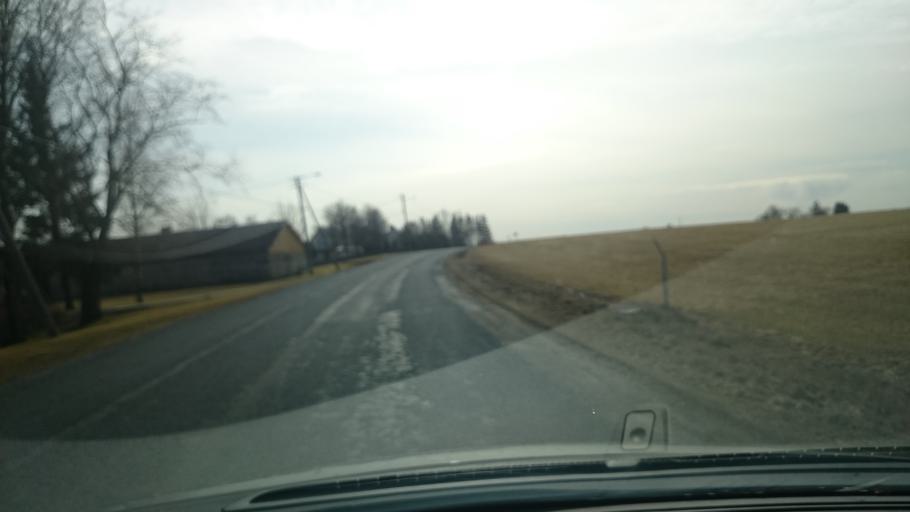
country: EE
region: Jaervamaa
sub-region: Tueri vald
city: Tueri
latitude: 58.8993
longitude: 25.4559
